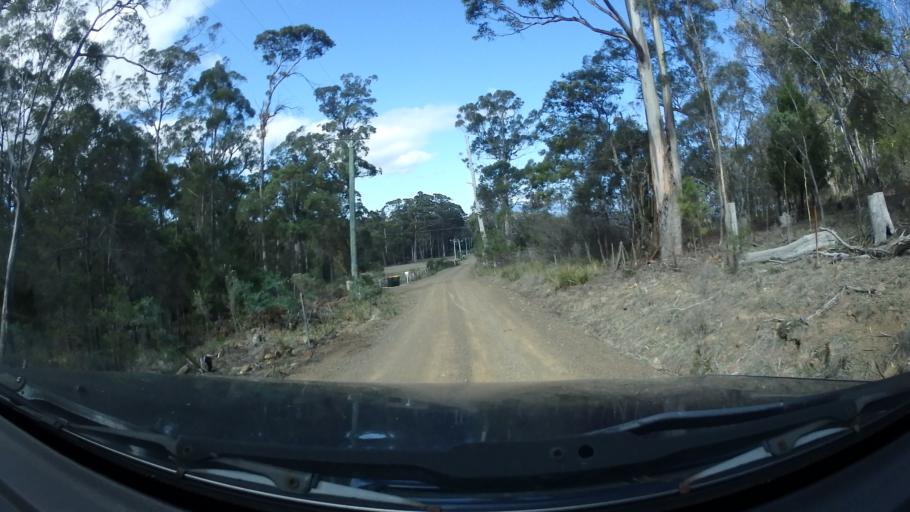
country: AU
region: Tasmania
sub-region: Sorell
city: Sorell
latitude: -42.5376
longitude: 147.8703
